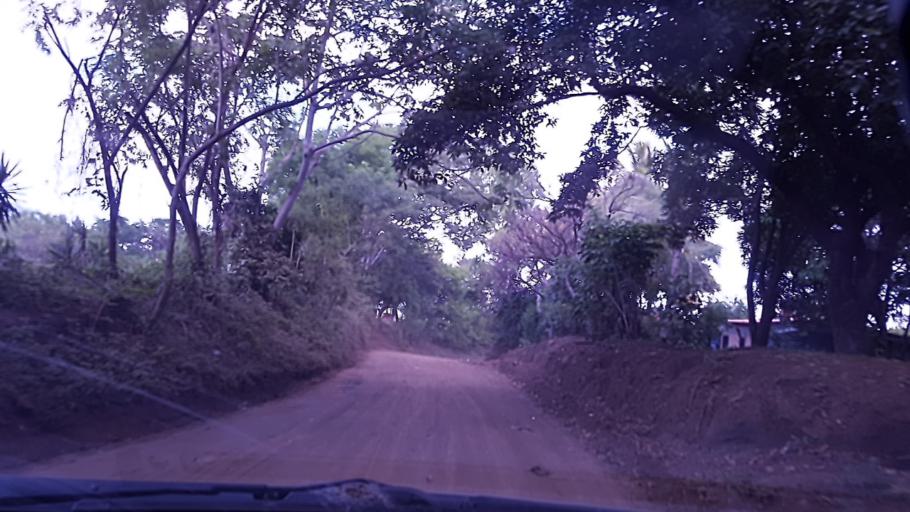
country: NI
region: Masaya
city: Ticuantepe
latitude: 11.9990
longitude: -86.2224
